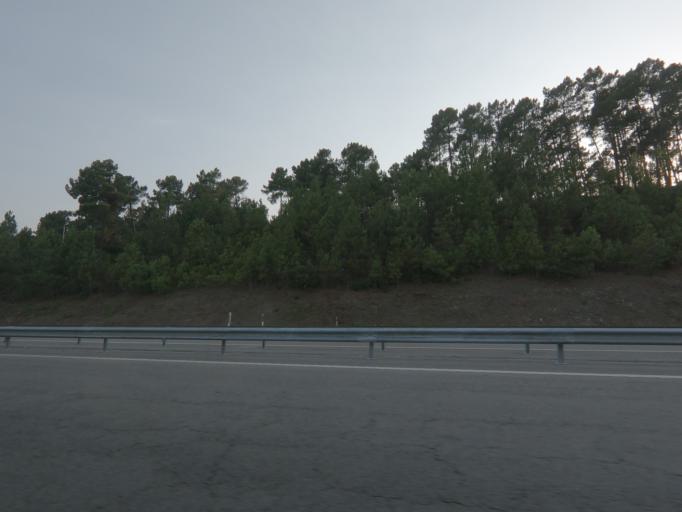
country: PT
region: Vila Real
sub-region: Santa Marta de Penaguiao
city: Santa Marta de Penaguiao
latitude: 41.2176
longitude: -7.7354
